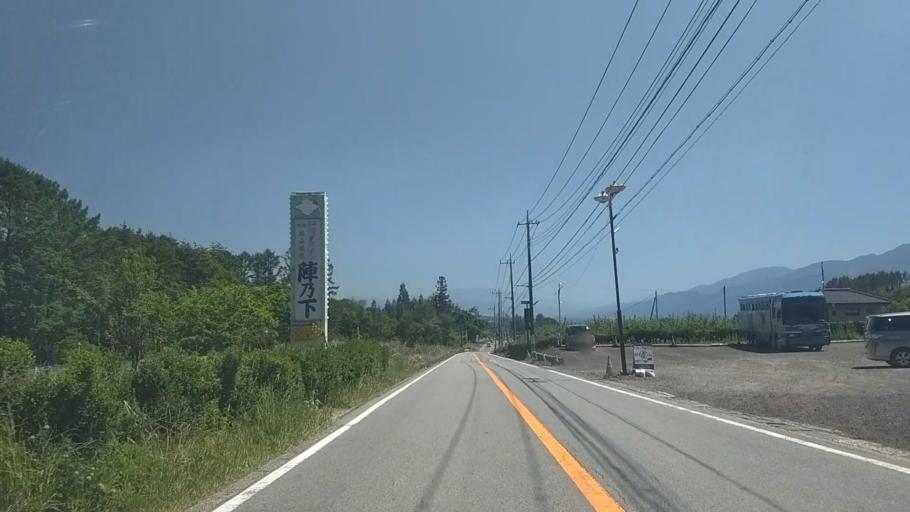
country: JP
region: Yamanashi
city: Nirasaki
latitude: 35.8550
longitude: 138.4312
